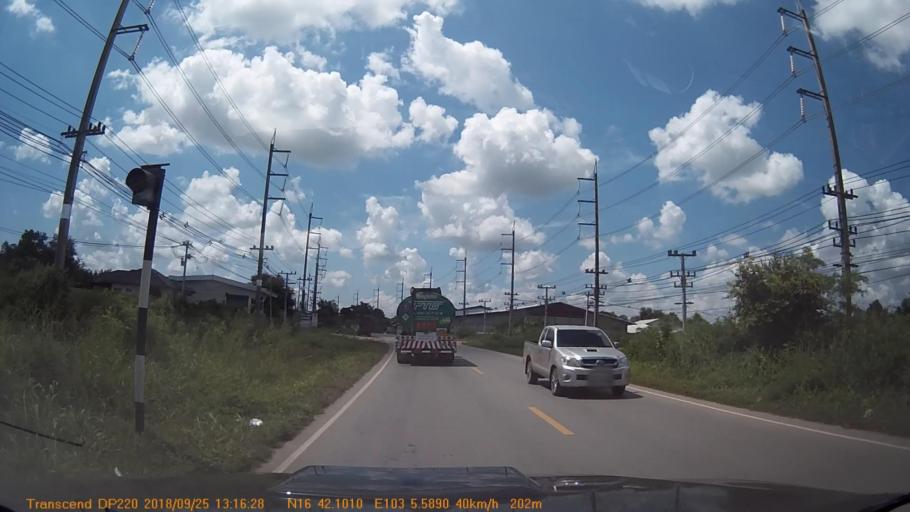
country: TH
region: Khon Kaen
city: Kranuan
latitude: 16.7017
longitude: 103.0931
